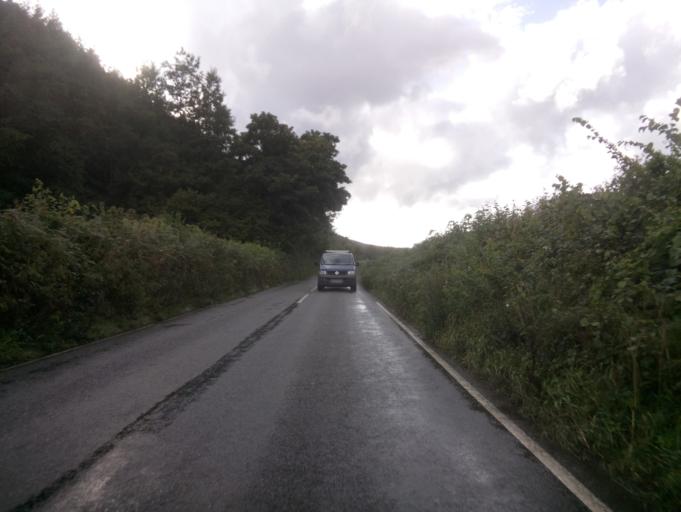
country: GB
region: England
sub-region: Devon
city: South Brent
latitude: 50.4115
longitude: -3.8166
